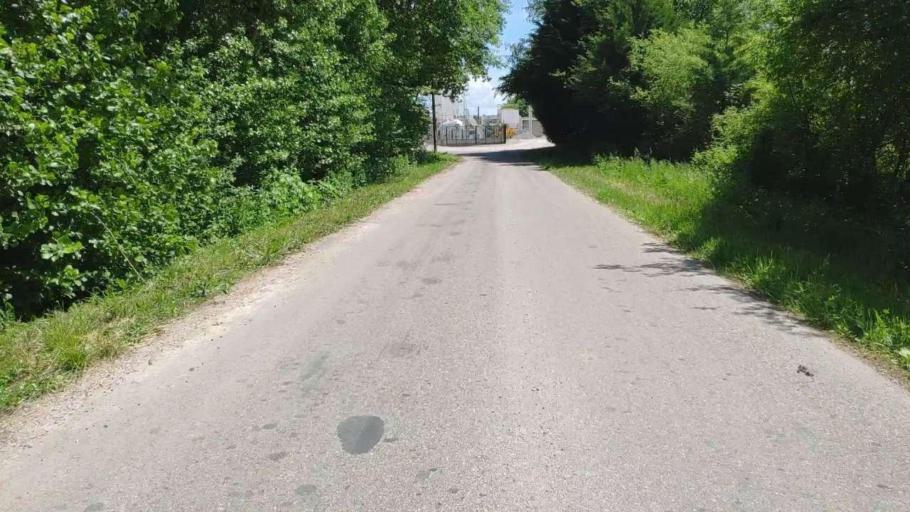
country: FR
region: Franche-Comte
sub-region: Departement du Jura
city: Bletterans
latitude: 46.7903
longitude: 5.4483
